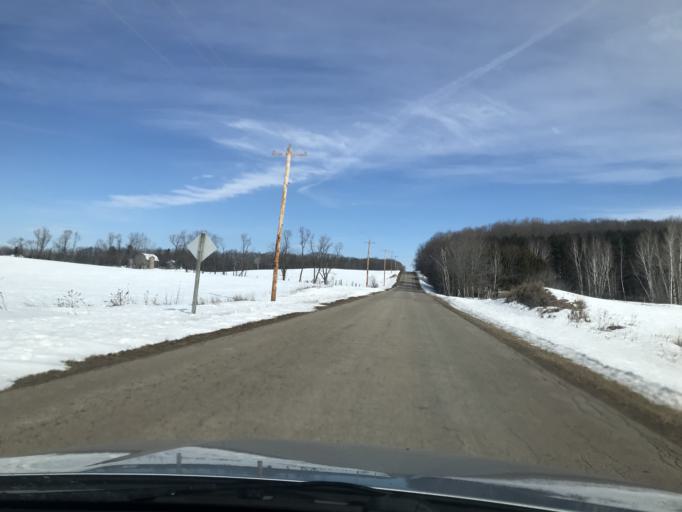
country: US
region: Wisconsin
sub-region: Oconto County
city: Gillett
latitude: 44.9642
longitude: -88.3061
